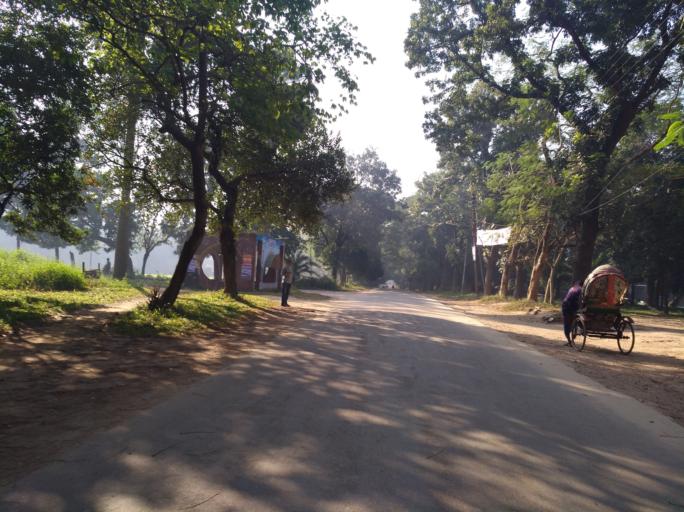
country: BD
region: Dhaka
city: Tungi
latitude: 23.8901
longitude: 90.2679
